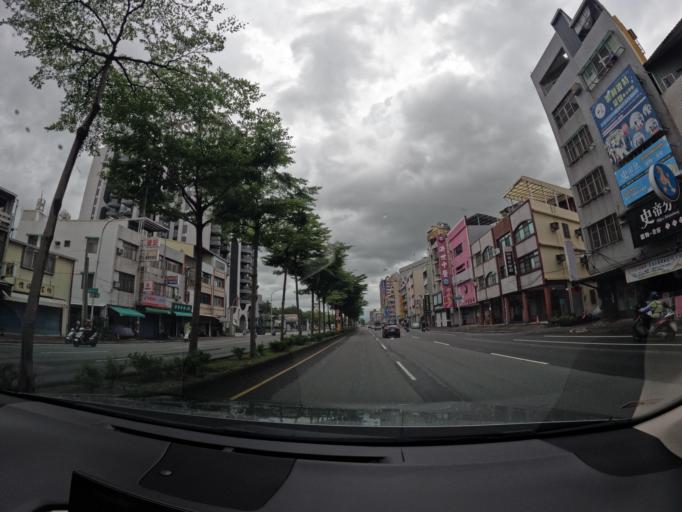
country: TW
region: Taiwan
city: Fengshan
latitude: 22.6240
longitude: 120.3703
